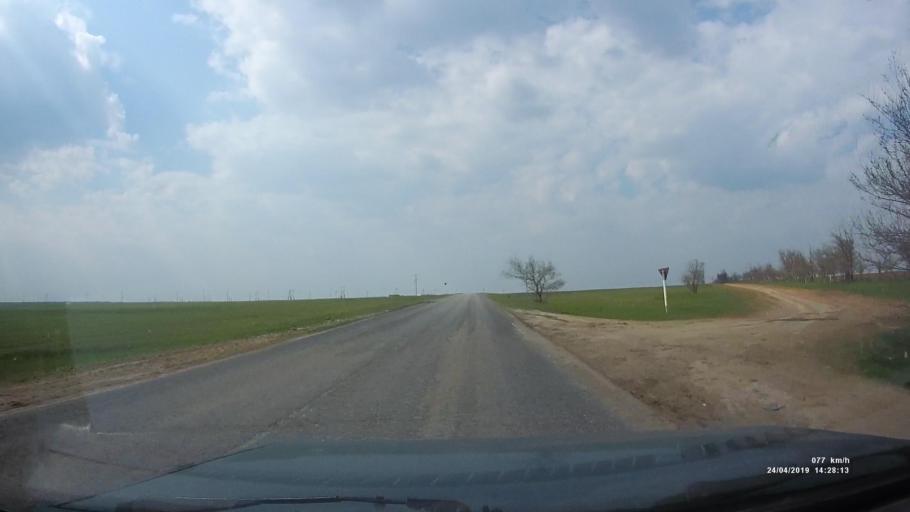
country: RU
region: Kalmykiya
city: Arshan'
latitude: 46.3374
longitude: 44.0325
